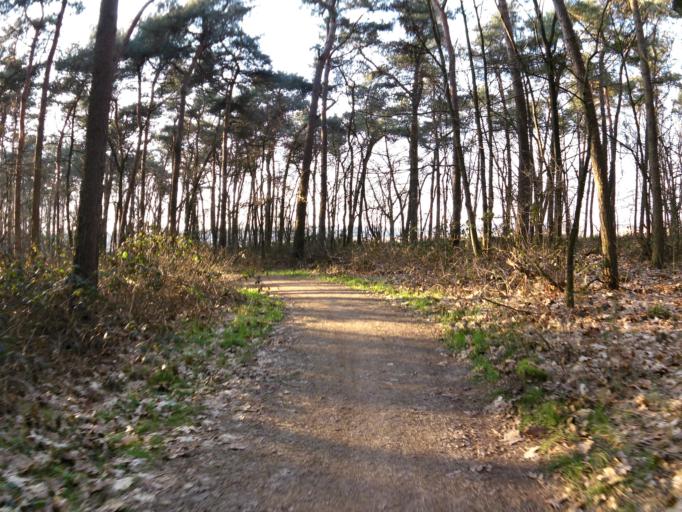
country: NL
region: North Brabant
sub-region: Gemeente Maasdonk
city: Geffen
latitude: 51.7050
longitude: 5.4086
